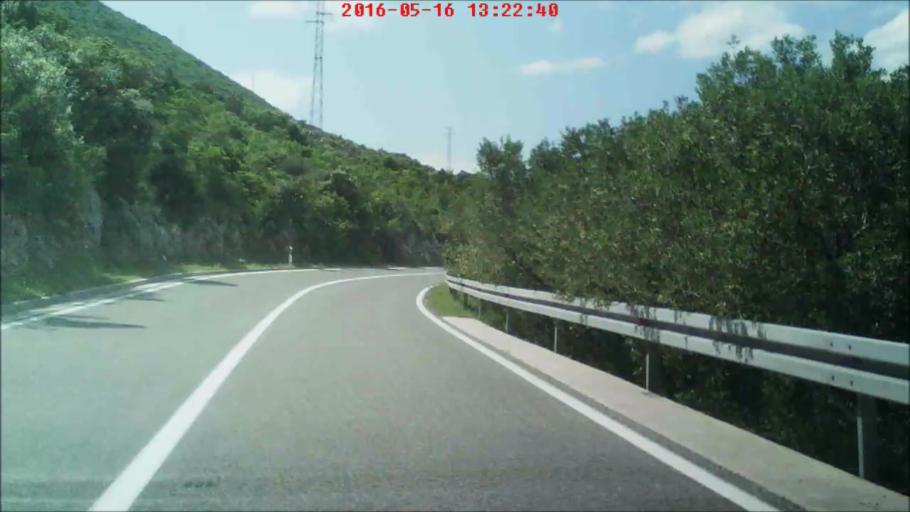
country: HR
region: Dubrovacko-Neretvanska
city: Ston
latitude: 42.8368
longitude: 17.7204
